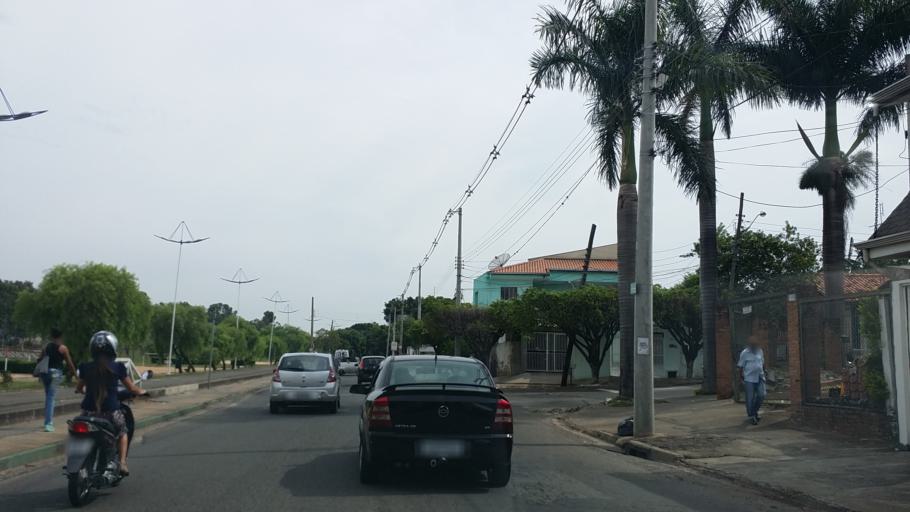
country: BR
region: Sao Paulo
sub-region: Indaiatuba
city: Indaiatuba
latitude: -23.1171
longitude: -47.2320
